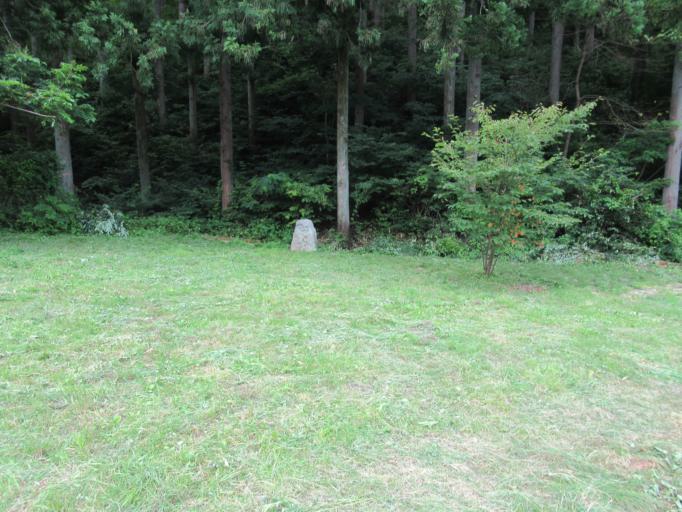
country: JP
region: Nagano
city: Shiojiri
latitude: 36.0305
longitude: 137.8750
